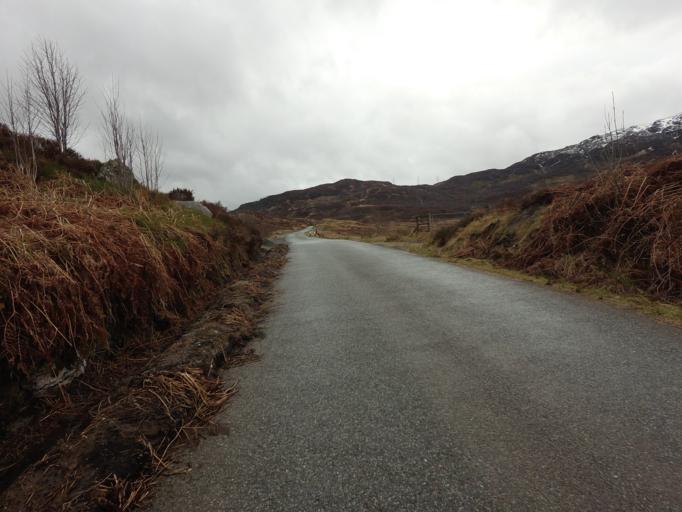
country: GB
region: Scotland
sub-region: West Dunbartonshire
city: Balloch
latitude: 56.2510
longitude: -4.5880
